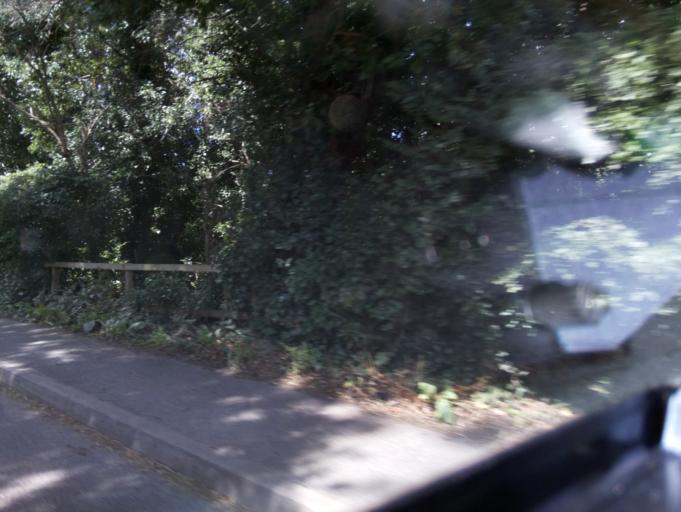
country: GB
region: England
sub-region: Nottinghamshire
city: Lowdham
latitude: 53.0130
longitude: -1.0111
